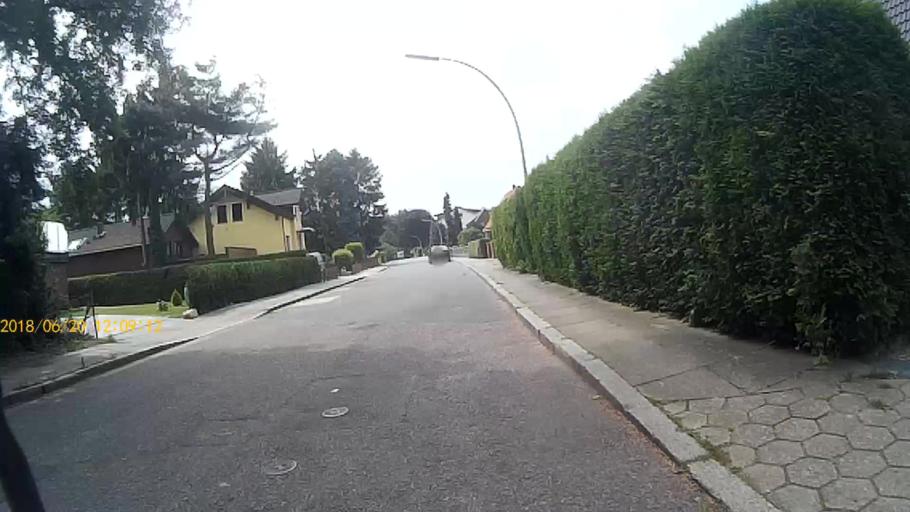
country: DE
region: Hamburg
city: Harburg
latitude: 53.4825
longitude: 10.0080
